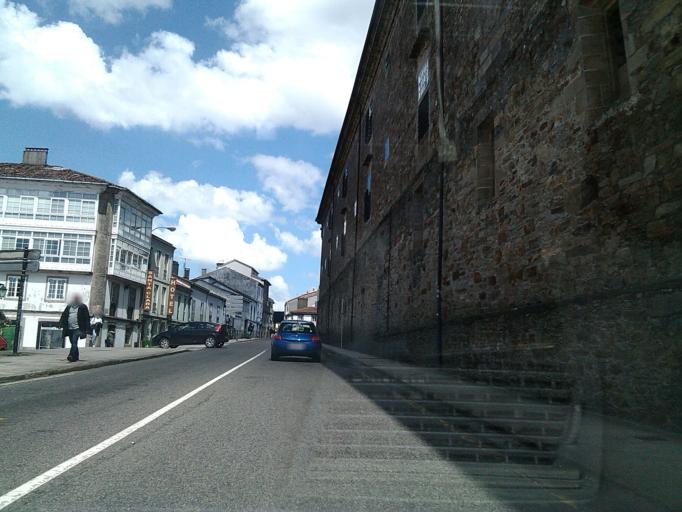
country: ES
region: Galicia
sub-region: Provincia da Coruna
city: Santiago de Compostela
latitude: 42.8852
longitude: -8.5411
